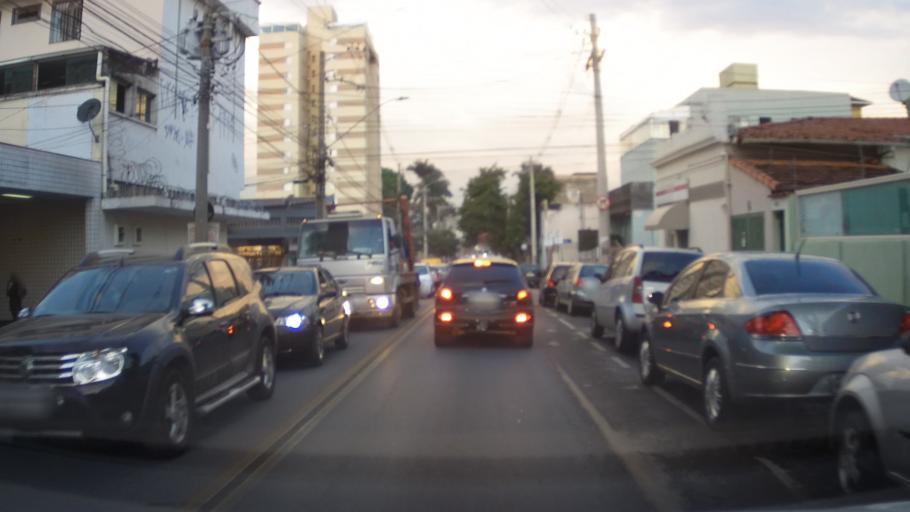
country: BR
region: Minas Gerais
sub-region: Belo Horizonte
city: Belo Horizonte
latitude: -19.9279
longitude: -43.9795
